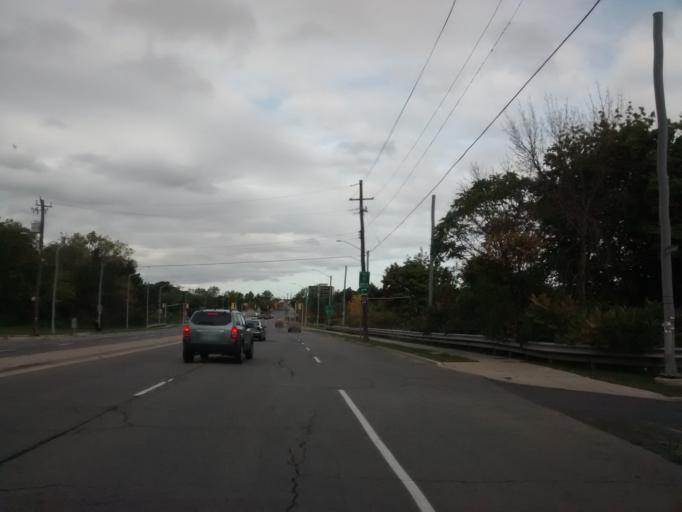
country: CA
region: Ontario
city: Hamilton
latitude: 43.2318
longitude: -79.7814
